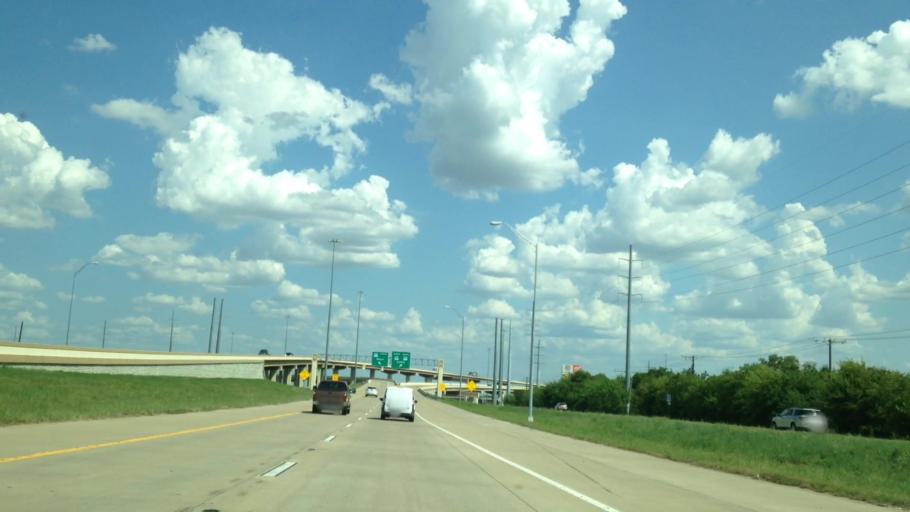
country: US
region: Texas
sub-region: Travis County
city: Pflugerville
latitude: 30.4768
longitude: -97.5993
